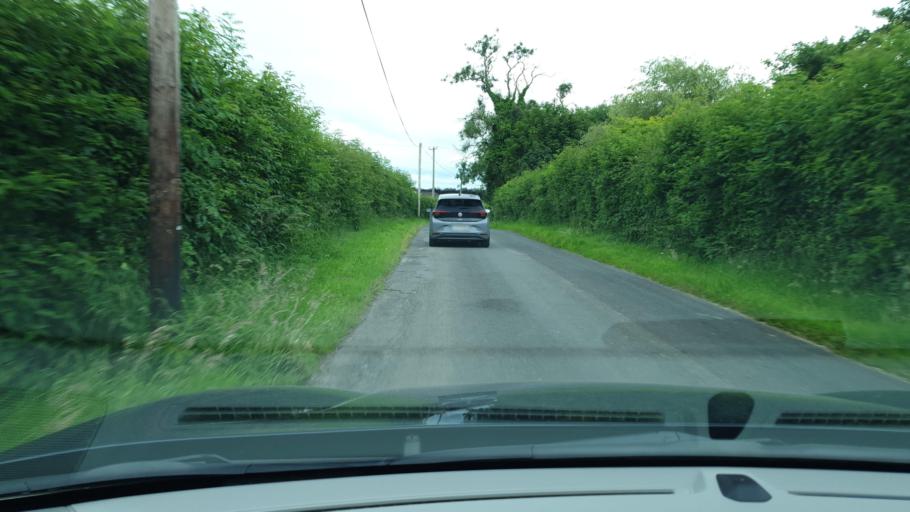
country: IE
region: Leinster
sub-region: An Mhi
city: Dunshaughlin
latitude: 53.5246
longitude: -6.5248
